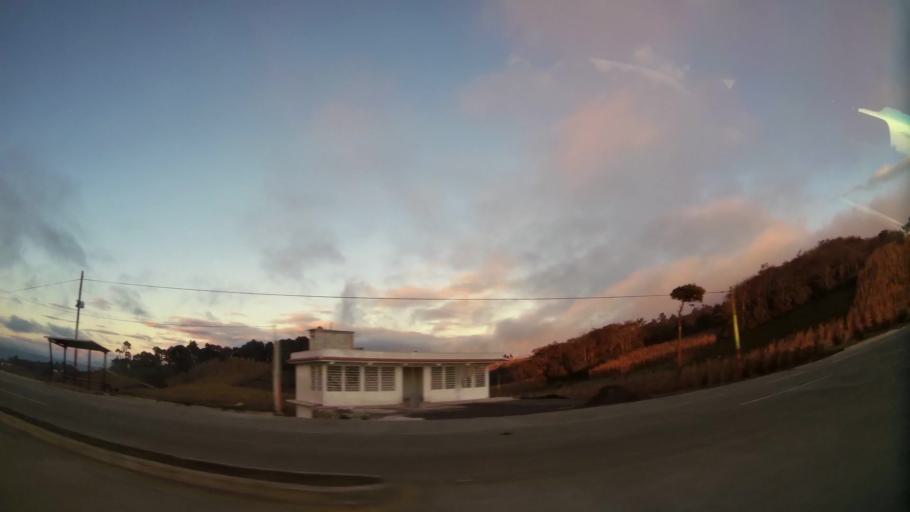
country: GT
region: Solola
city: Concepcion
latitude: 14.8355
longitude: -91.1150
